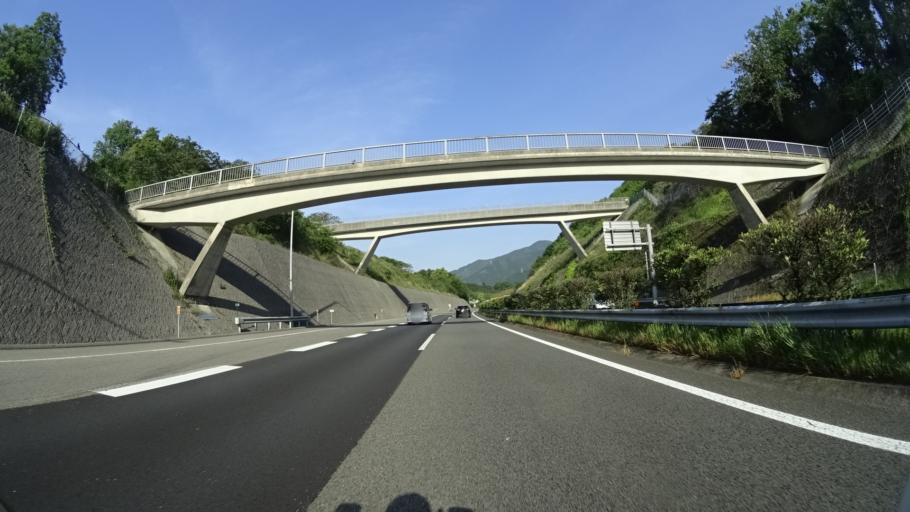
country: JP
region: Ehime
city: Saijo
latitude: 33.9122
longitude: 133.2406
